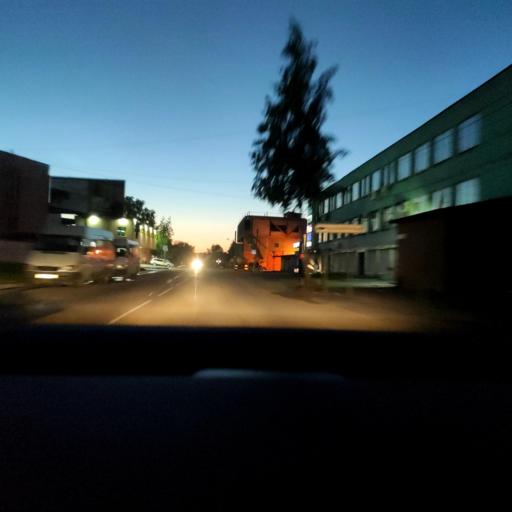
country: RU
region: Moskovskaya
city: Reutov
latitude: 55.7675
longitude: 37.8807
